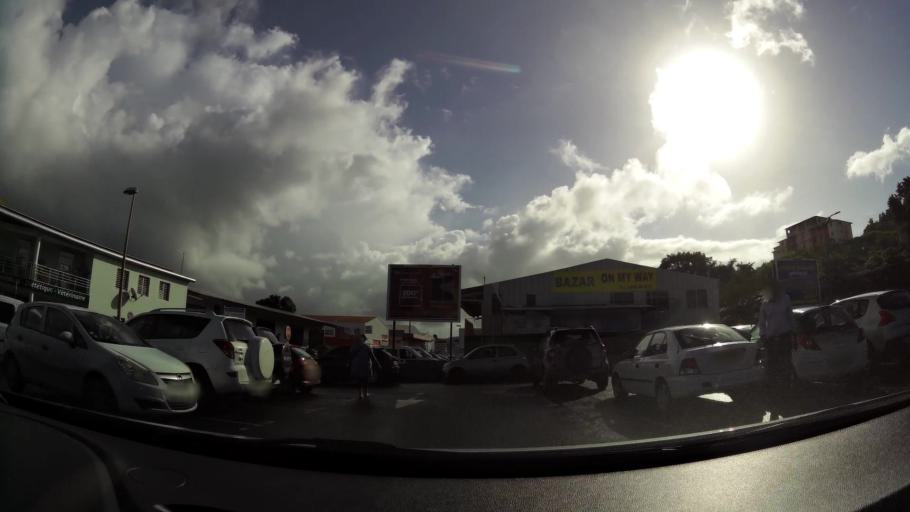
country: MQ
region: Martinique
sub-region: Martinique
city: Ducos
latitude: 14.5246
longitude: -60.9802
